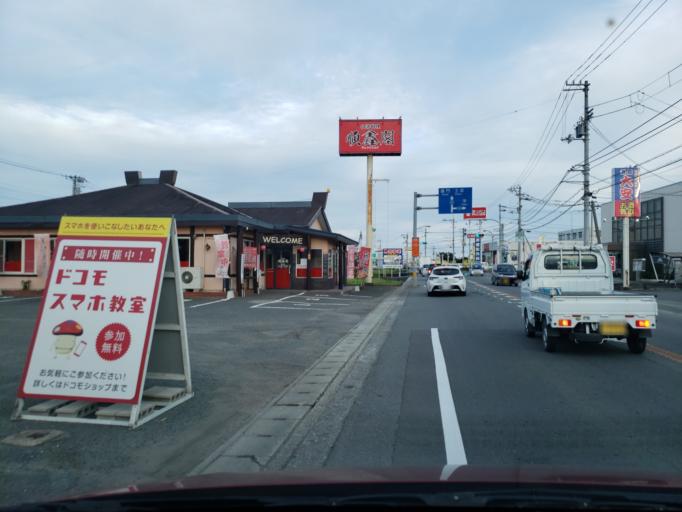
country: JP
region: Tokushima
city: Kamojimacho-jogejima
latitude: 34.0842
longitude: 134.2803
